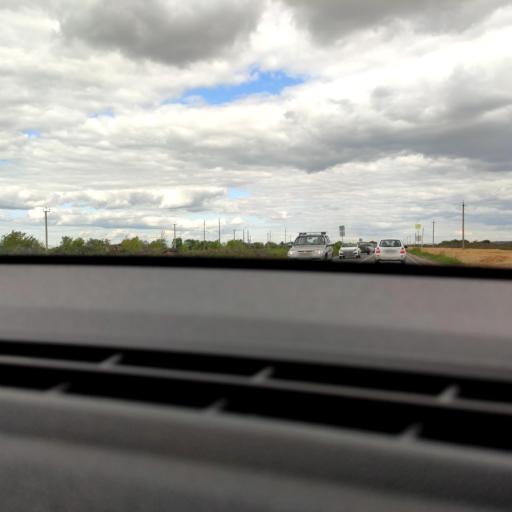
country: RU
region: Samara
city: Podstepki
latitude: 53.5662
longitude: 49.1408
